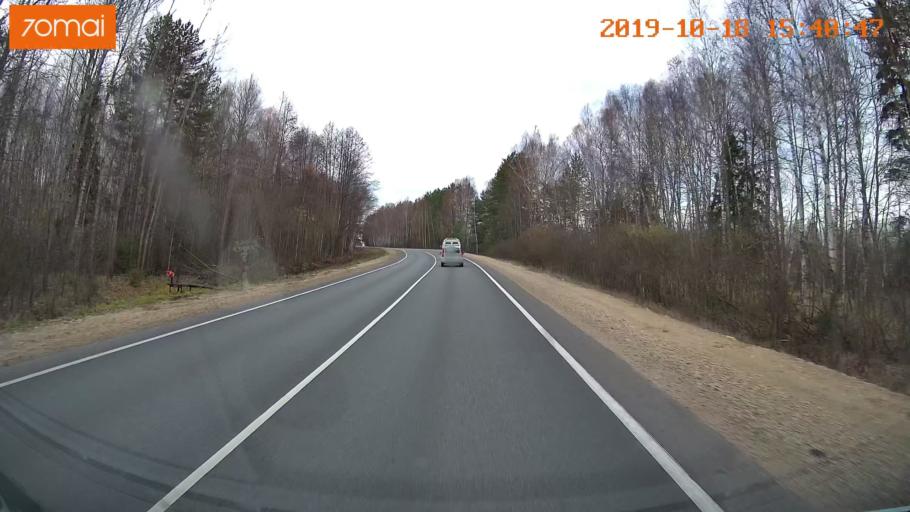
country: RU
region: Vladimir
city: Golovino
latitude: 55.9387
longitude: 40.5914
